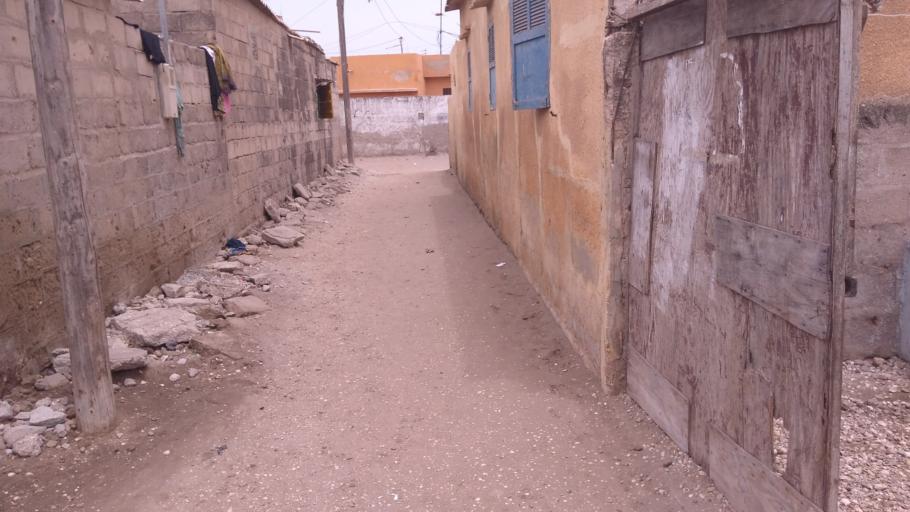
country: SN
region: Dakar
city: Pikine
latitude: 14.6877
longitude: -17.2262
